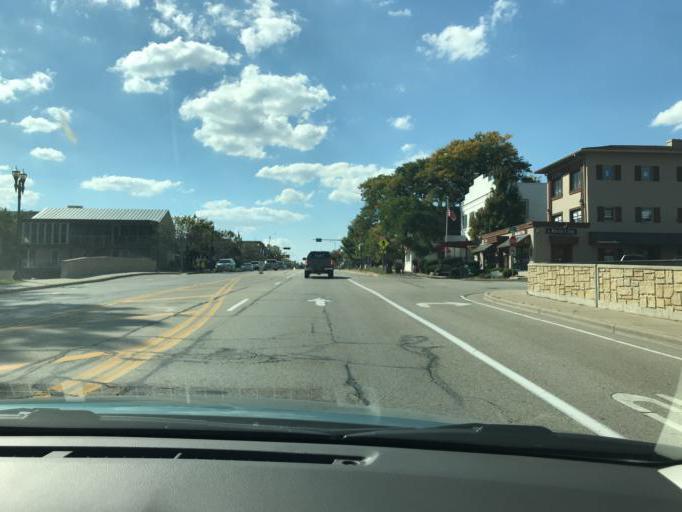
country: US
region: Wisconsin
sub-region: Walworth County
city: Lake Geneva
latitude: 42.5917
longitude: -88.4314
